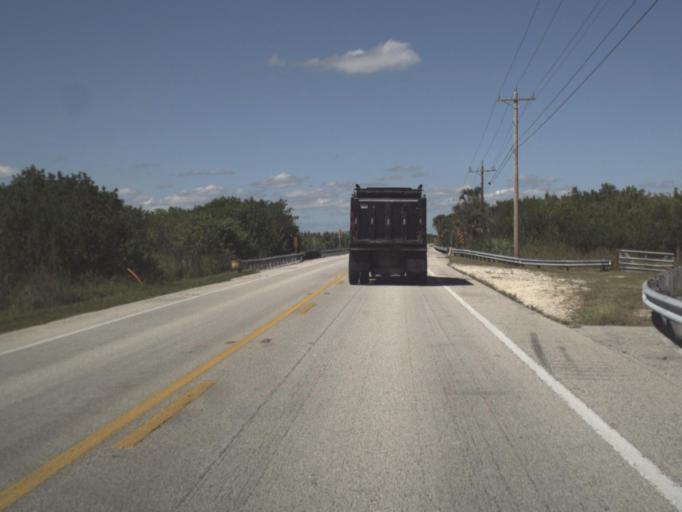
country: US
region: Florida
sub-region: Collier County
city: Marco
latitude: 25.9374
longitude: -81.4592
